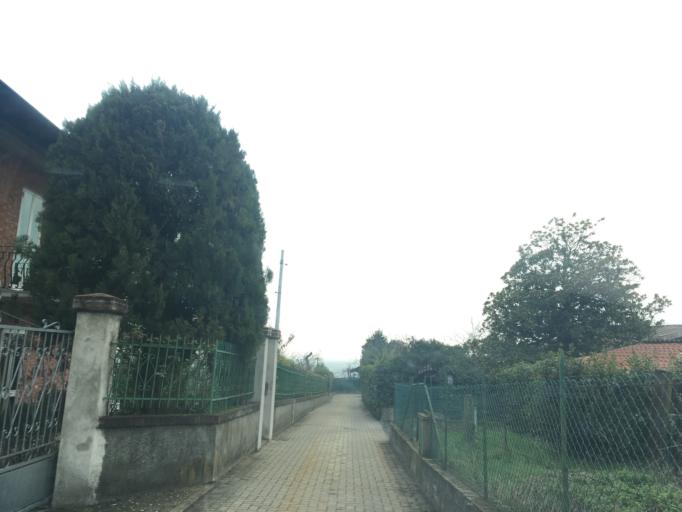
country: IT
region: Piedmont
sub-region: Provincia di Torino
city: Moncalieri
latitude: 45.0249
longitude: 7.6798
